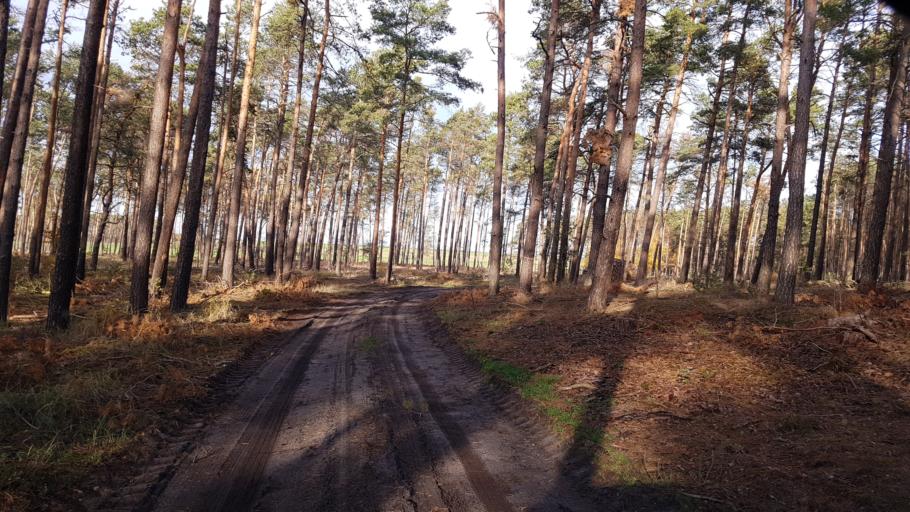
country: DE
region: Brandenburg
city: Trobitz
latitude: 51.6492
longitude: 13.4199
